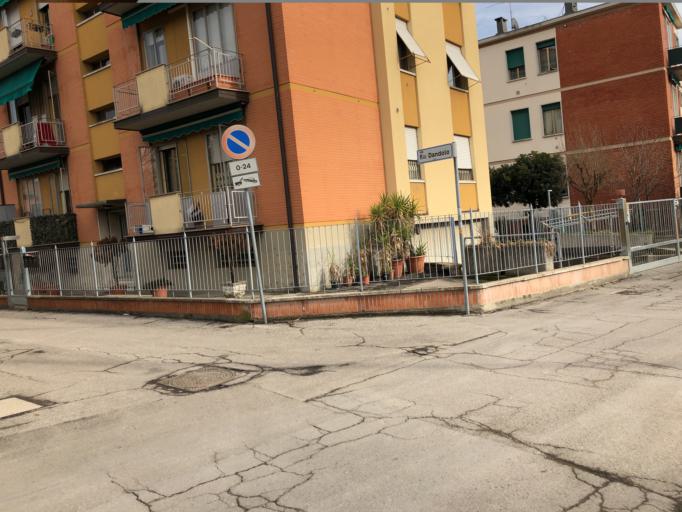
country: IT
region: Emilia-Romagna
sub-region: Provincia di Bologna
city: Trebbo
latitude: 44.5218
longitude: 11.2932
